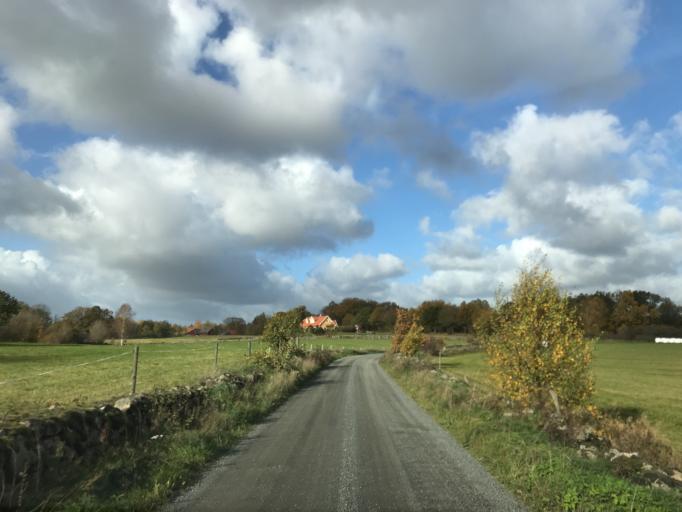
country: SE
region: Skane
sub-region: Perstorps Kommun
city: Perstorp
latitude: 56.0238
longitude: 13.3893
